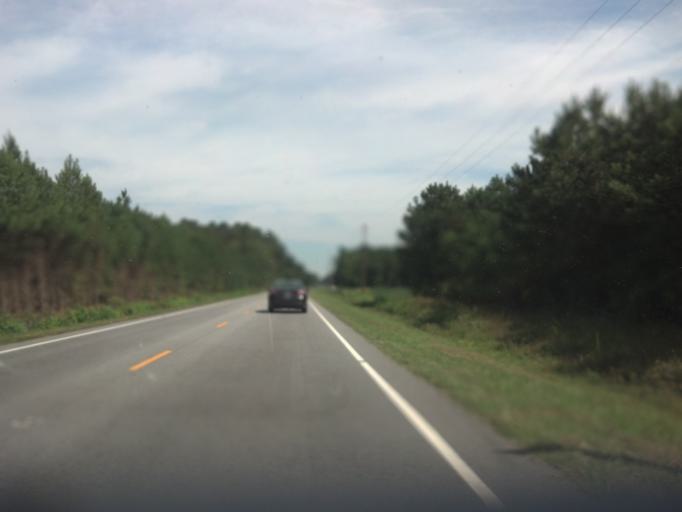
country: US
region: North Carolina
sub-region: Greene County
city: Maury
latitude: 35.4969
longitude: -77.6269
